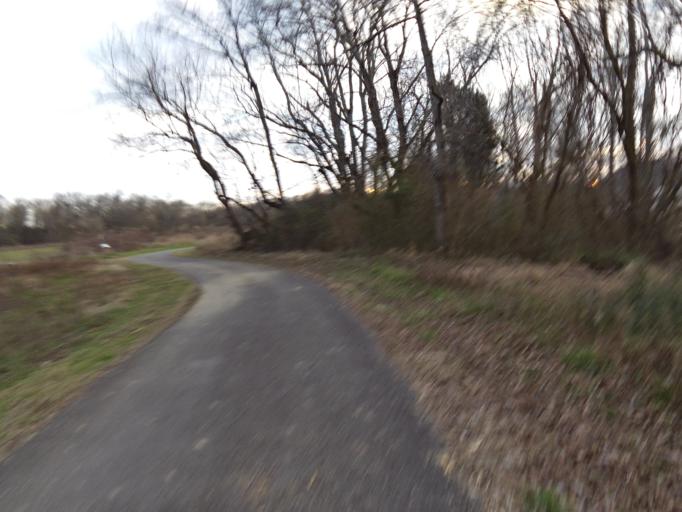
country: US
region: Tennessee
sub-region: Knox County
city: Knoxville
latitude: 35.9565
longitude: -83.8519
